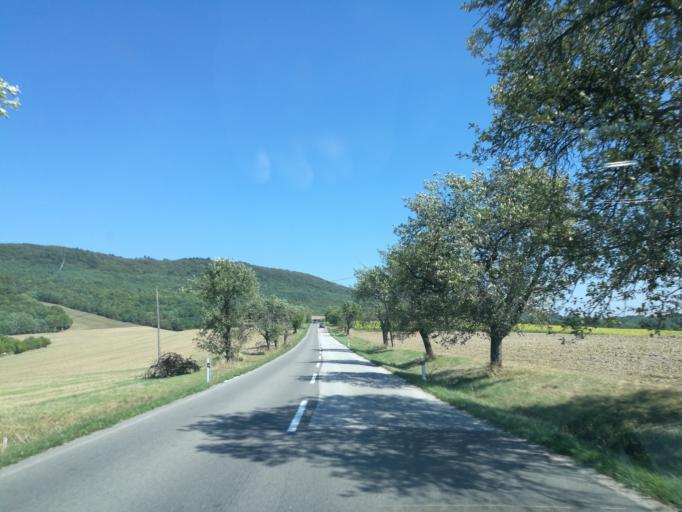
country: SK
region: Nitriansky
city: Brezova pod Bradlom
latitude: 48.6665
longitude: 17.5490
